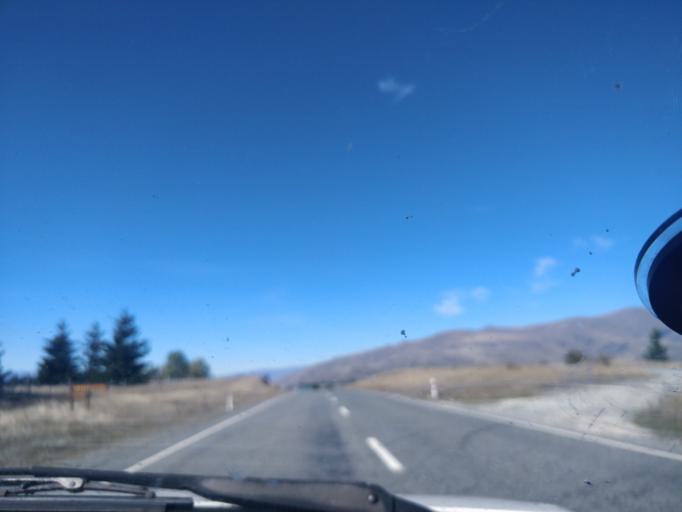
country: NZ
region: Otago
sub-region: Queenstown-Lakes District
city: Wanaka
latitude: -44.2703
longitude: 170.0442
